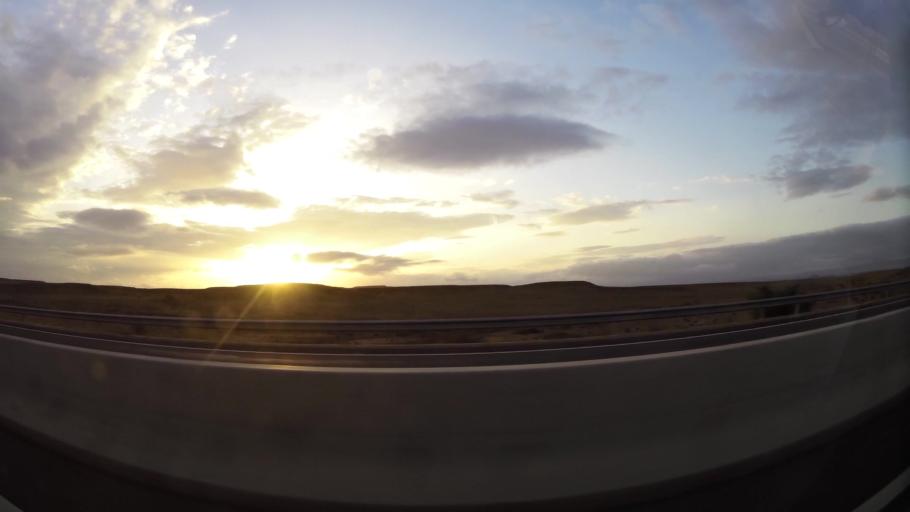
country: MA
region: Oriental
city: Taourirt
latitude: 34.5040
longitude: -2.9517
